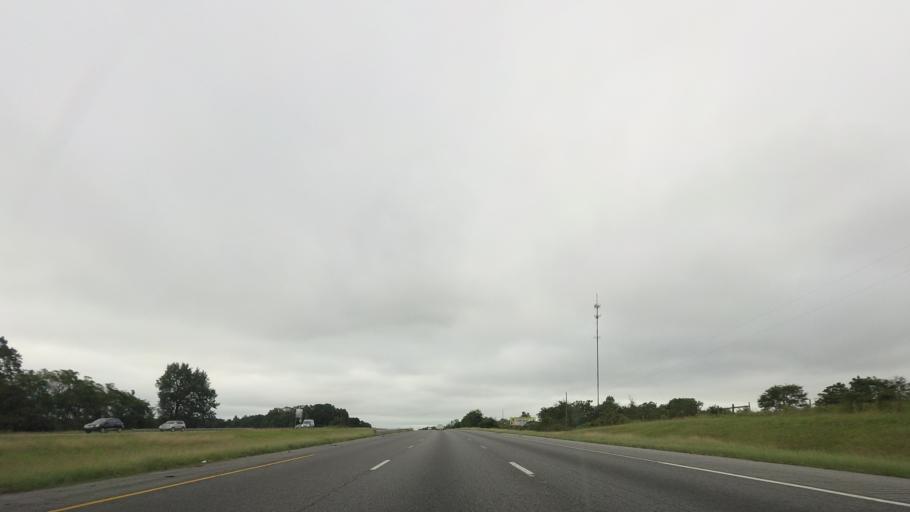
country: US
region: Georgia
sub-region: Dooly County
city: Unadilla
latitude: 32.3455
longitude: -83.7690
